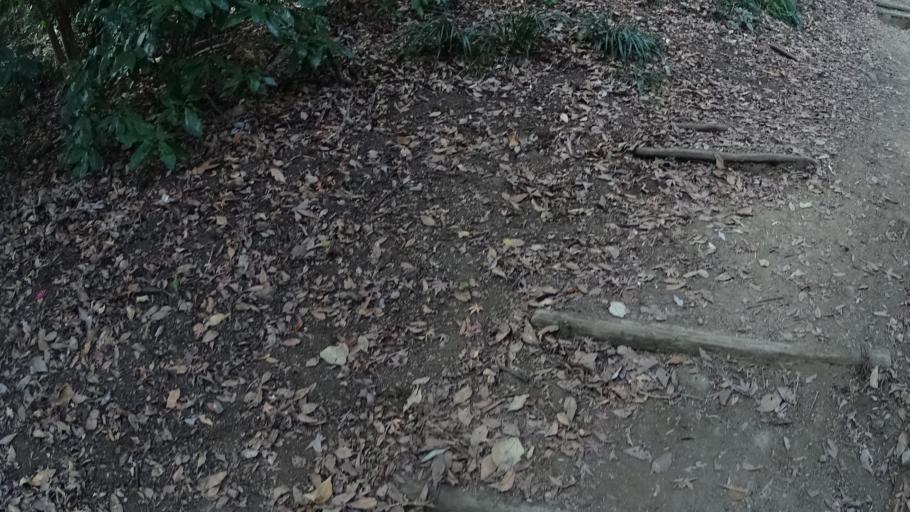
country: JP
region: Kanagawa
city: Hiratsuka
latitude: 35.3225
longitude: 139.3225
